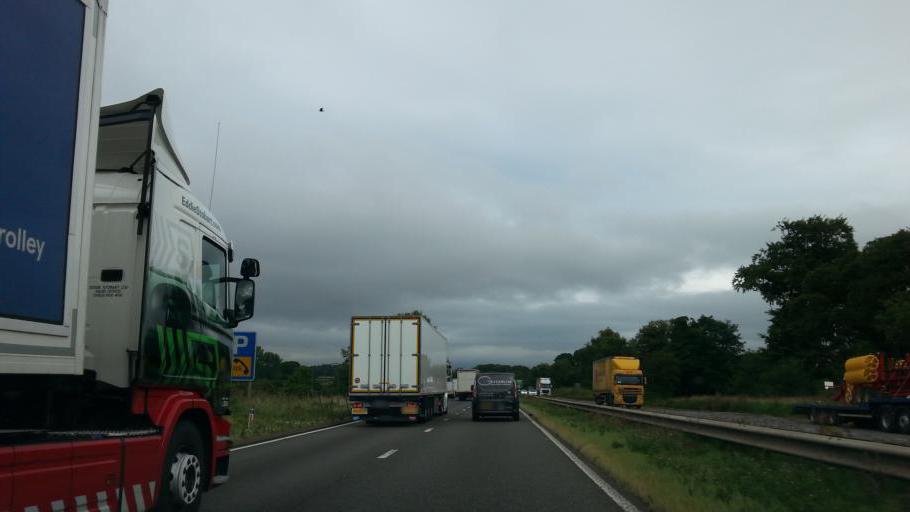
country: GB
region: England
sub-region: Nottinghamshire
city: Babworth
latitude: 53.3364
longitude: -1.0285
